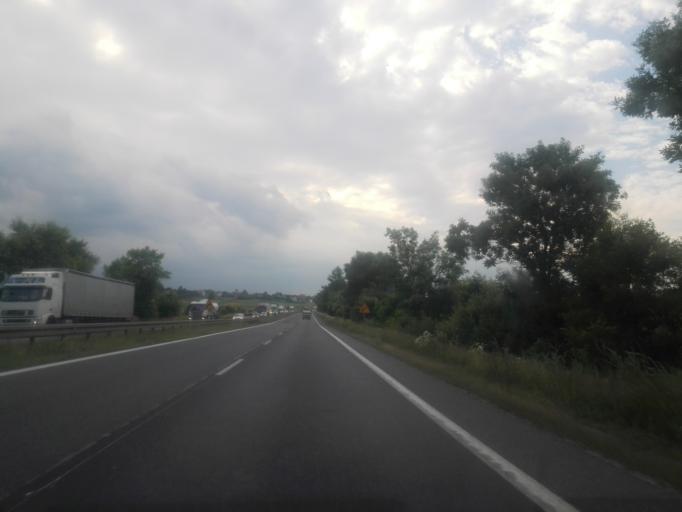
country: PL
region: Silesian Voivodeship
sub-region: Powiat bedzinski
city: Siewierz
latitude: 50.4912
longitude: 19.2097
